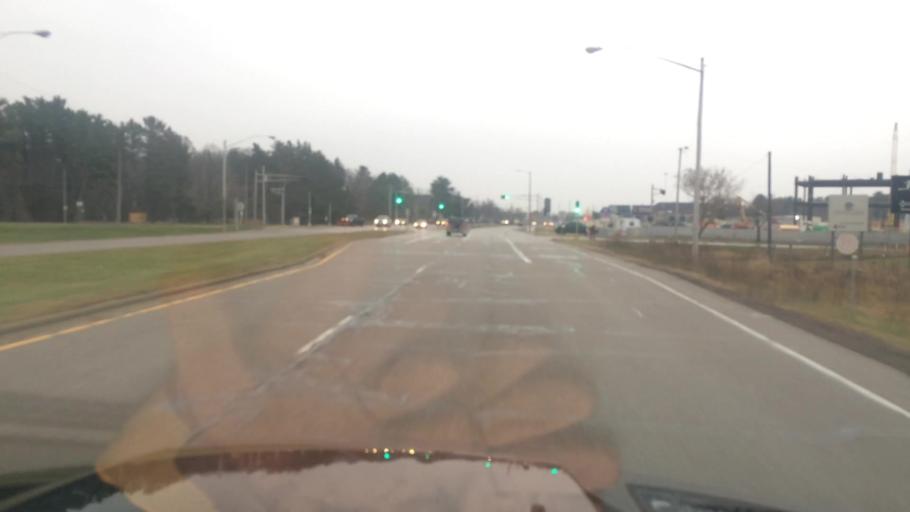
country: US
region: Wisconsin
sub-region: Portage County
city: Stevens Point
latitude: 44.5422
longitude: -89.5763
